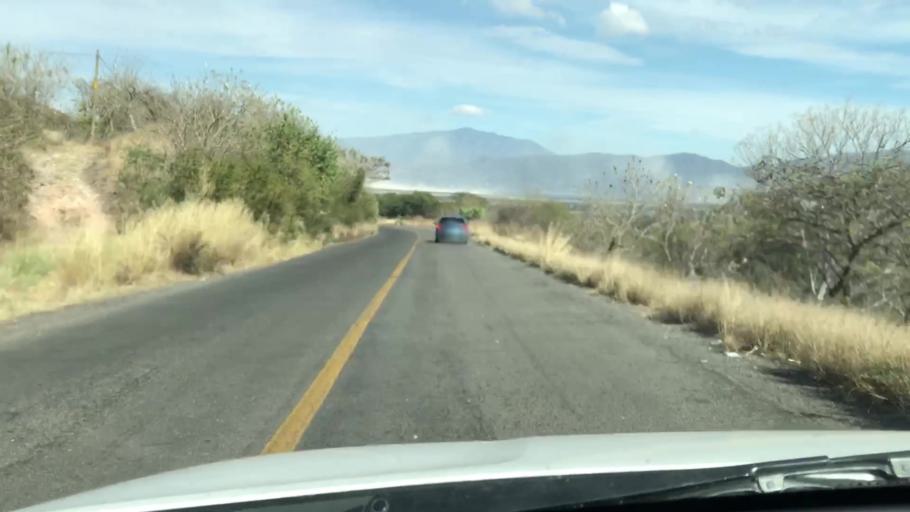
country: MX
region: Jalisco
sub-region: Zacoalco de Torres
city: Barranca de Otates (Barranca de Otatan)
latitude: 20.2591
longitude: -103.6534
